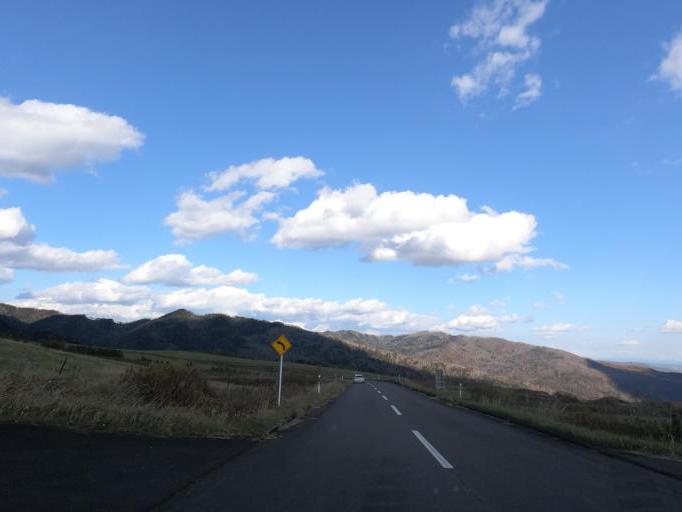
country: JP
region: Hokkaido
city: Otofuke
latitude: 43.2876
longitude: 143.1859
